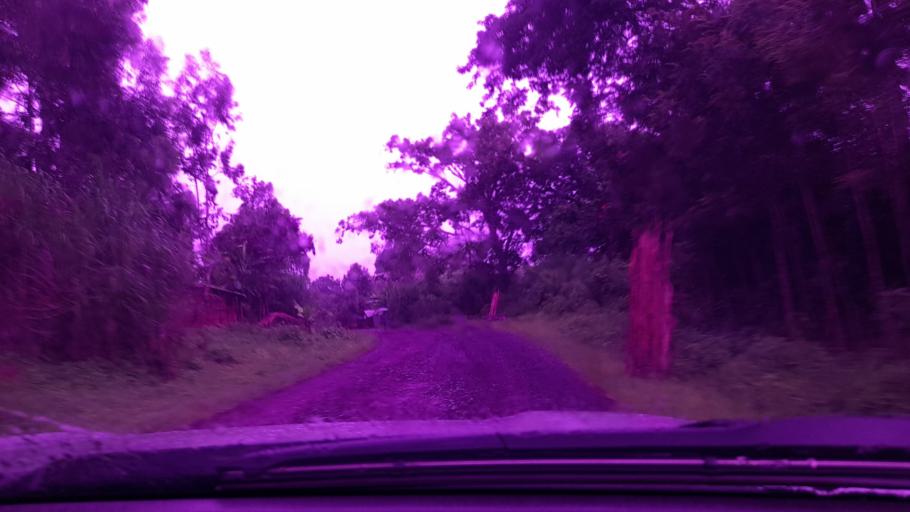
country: ET
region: Oromiya
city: Metu
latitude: 8.4567
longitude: 35.6372
